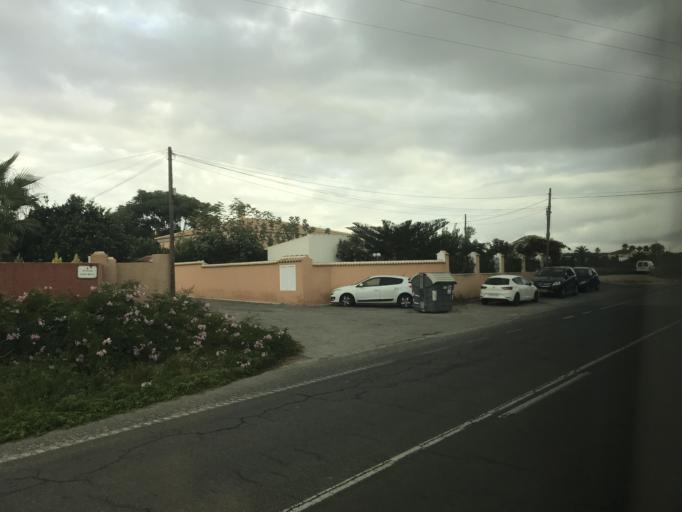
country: ES
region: Valencia
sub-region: Provincia de Alicante
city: Guardamar del Segura
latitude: 38.1291
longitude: -0.6503
